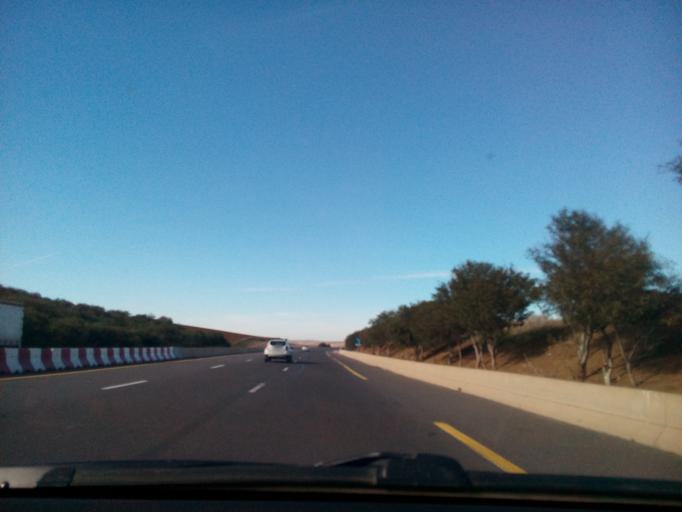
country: DZ
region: Tlemcen
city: Sidi Abdelli
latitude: 35.0313
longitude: -1.0156
